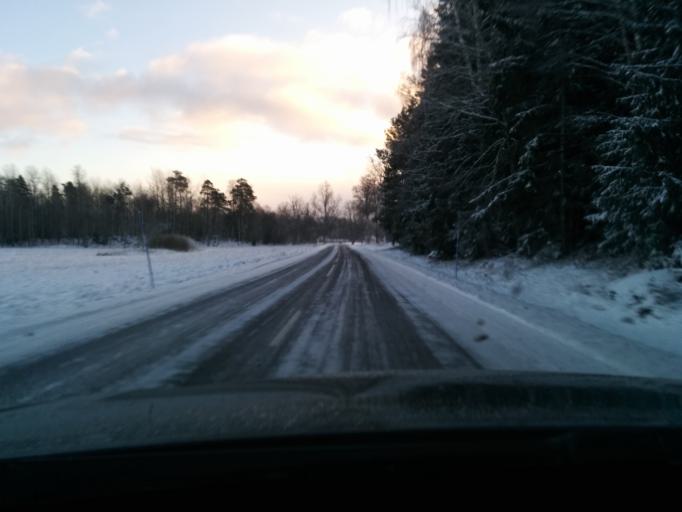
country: SE
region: Uppsala
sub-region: Tierps Kommun
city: Orbyhus
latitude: 60.2049
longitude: 17.6993
